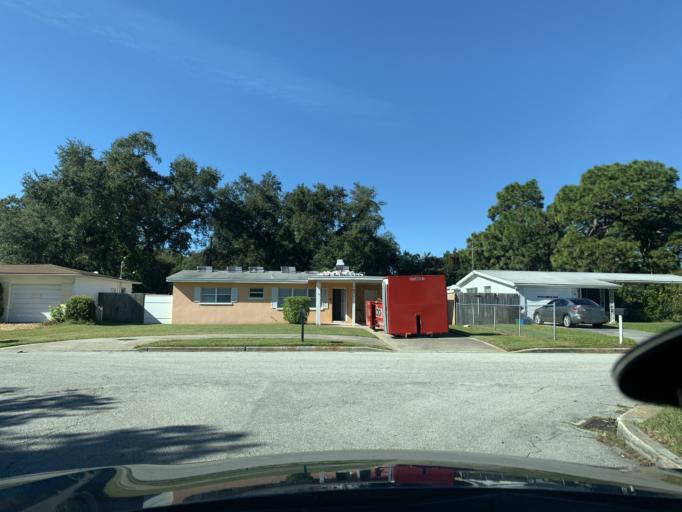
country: US
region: Florida
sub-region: Pinellas County
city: Gulfport
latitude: 27.7529
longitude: -82.7140
